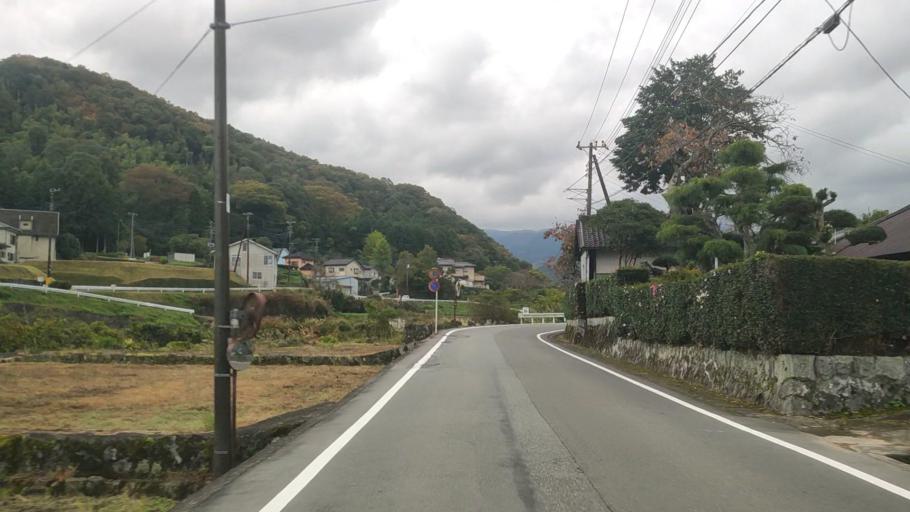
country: JP
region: Shizuoka
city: Ito
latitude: 34.9424
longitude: 138.9975
